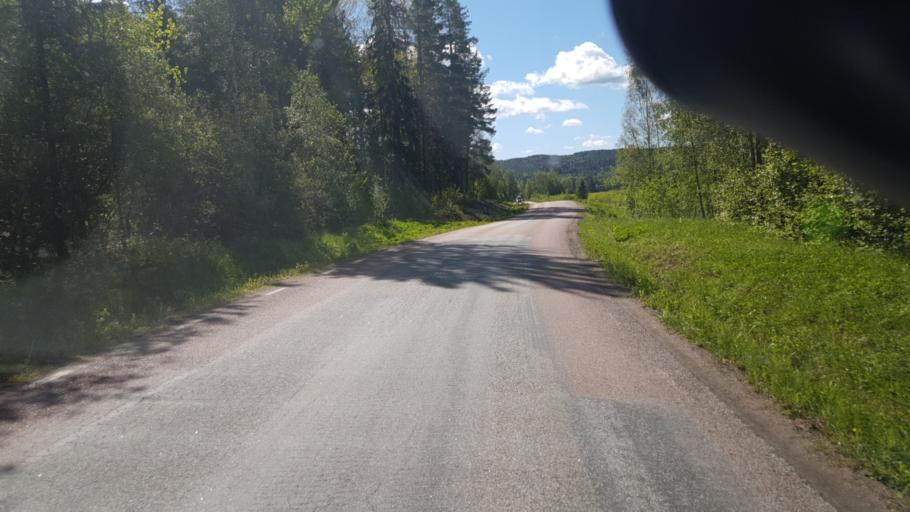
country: SE
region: Vaermland
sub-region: Arvika Kommun
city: Arvika
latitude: 59.5313
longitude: 12.8238
